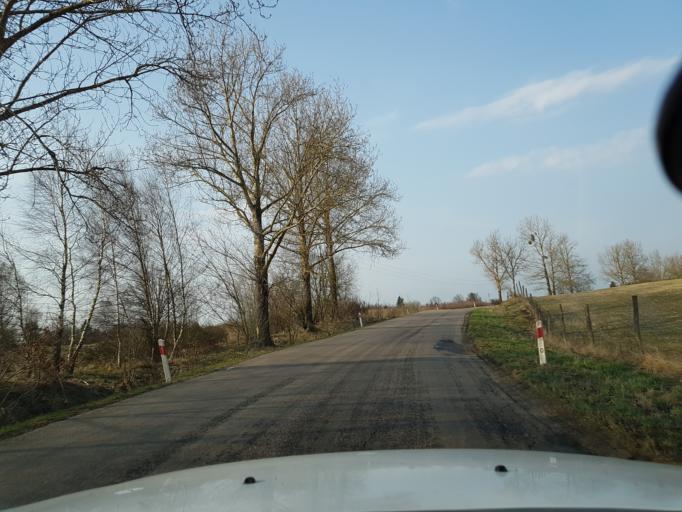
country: PL
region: West Pomeranian Voivodeship
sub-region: Powiat swidwinski
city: Polczyn-Zdroj
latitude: 53.7205
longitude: 16.0690
